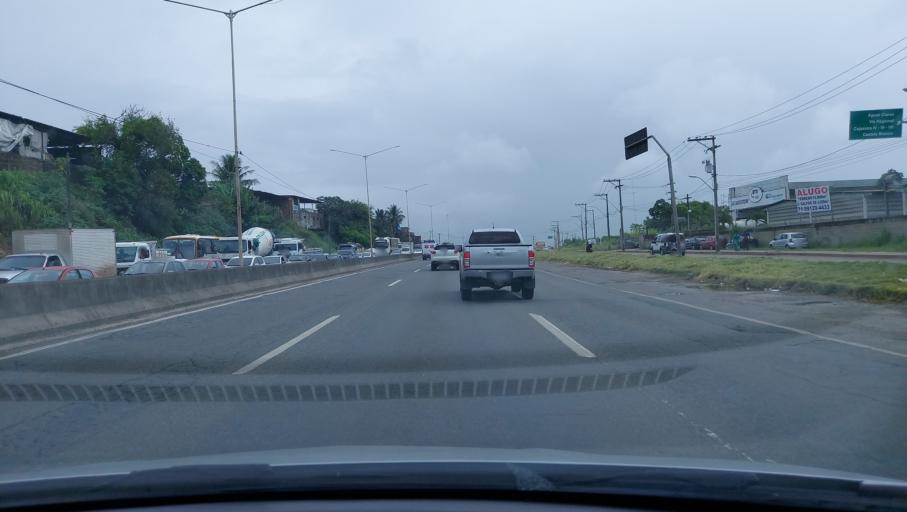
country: BR
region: Bahia
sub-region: Salvador
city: Salvador
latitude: -12.8932
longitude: -38.4468
